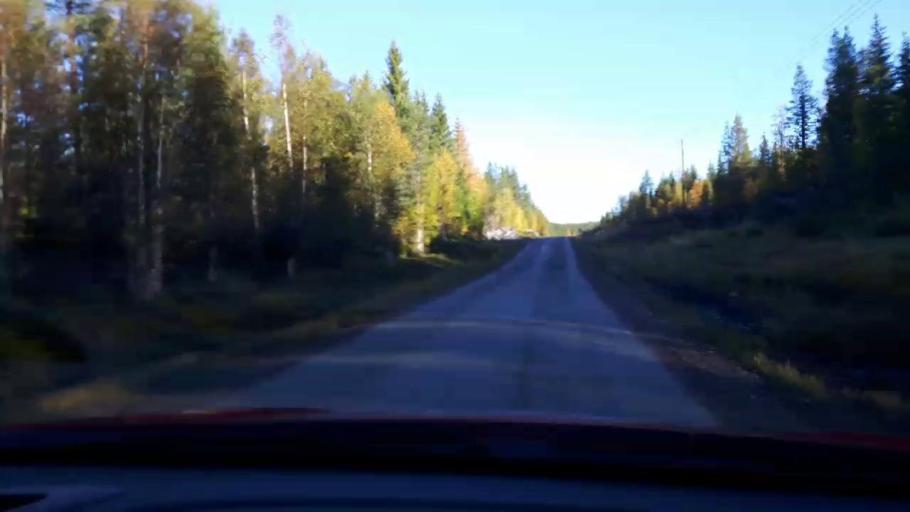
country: SE
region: Jaemtland
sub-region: Stroemsunds Kommun
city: Stroemsund
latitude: 64.3745
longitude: 15.1516
